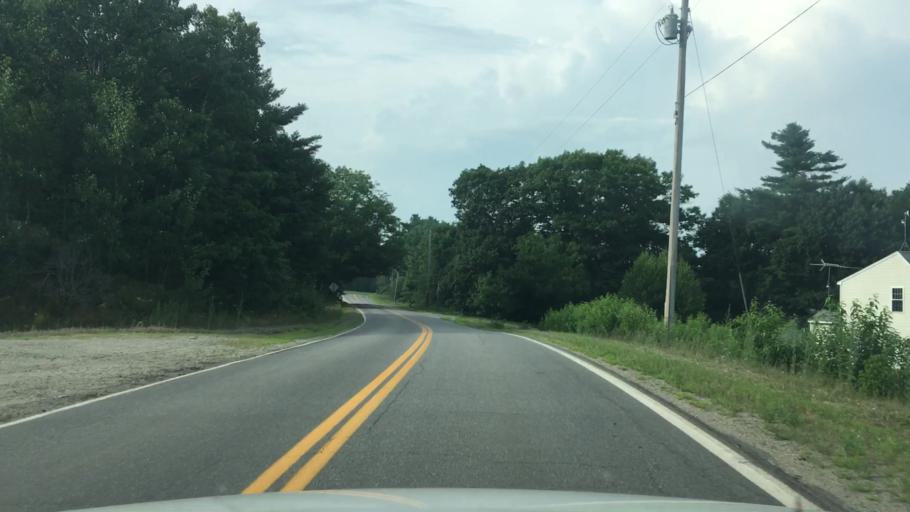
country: US
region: Maine
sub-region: Knox County
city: Washington
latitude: 44.2061
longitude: -69.3816
